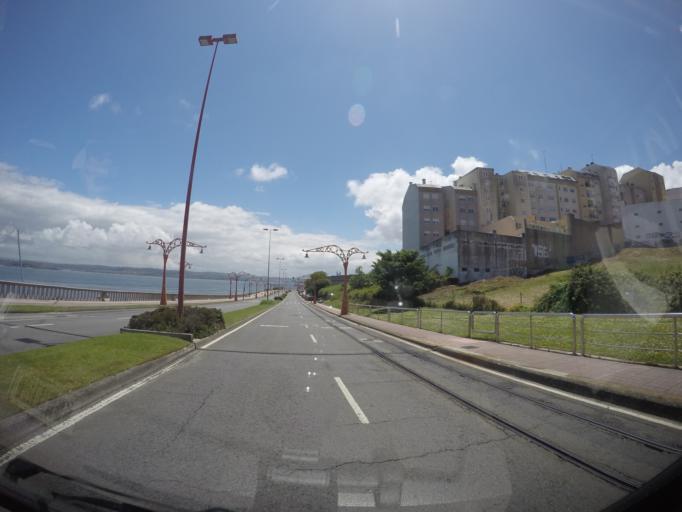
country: ES
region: Galicia
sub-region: Provincia da Coruna
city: A Coruna
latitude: 43.3804
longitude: -8.3969
